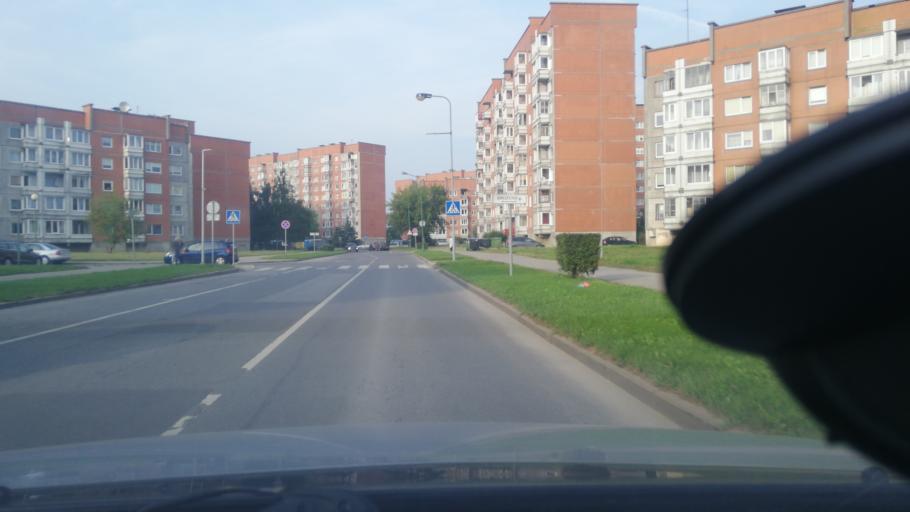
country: LT
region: Klaipedos apskritis
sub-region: Klaipeda
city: Klaipeda
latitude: 55.6654
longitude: 21.2007
